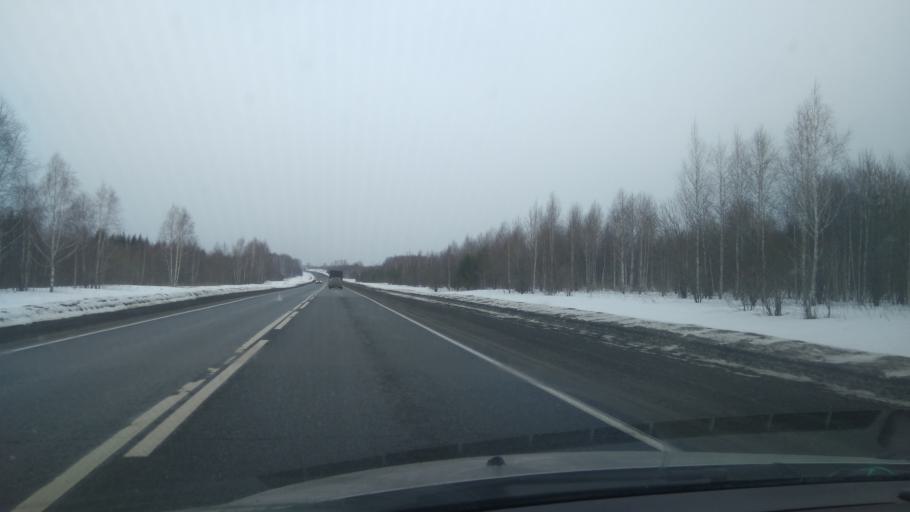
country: RU
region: Perm
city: Orda
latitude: 57.2283
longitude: 57.0726
